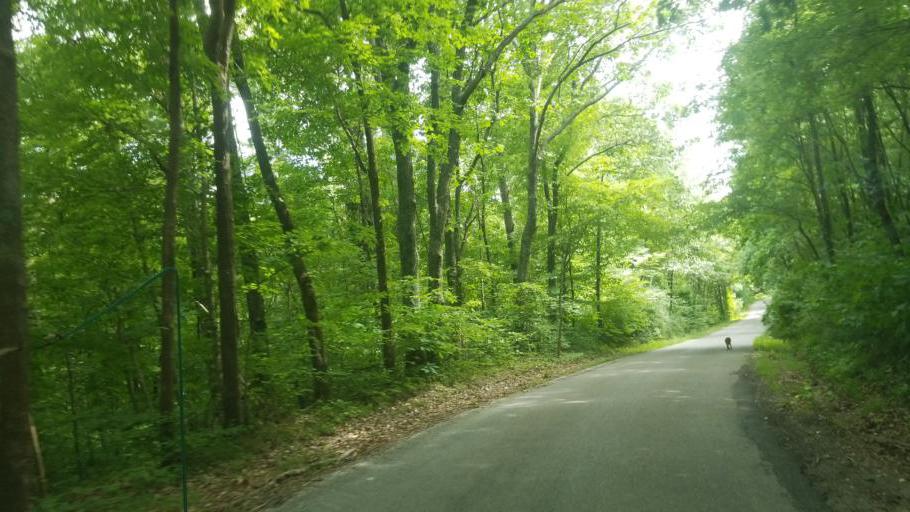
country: US
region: Illinois
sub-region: Union County
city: Cobden
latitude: 37.6217
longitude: -89.3687
